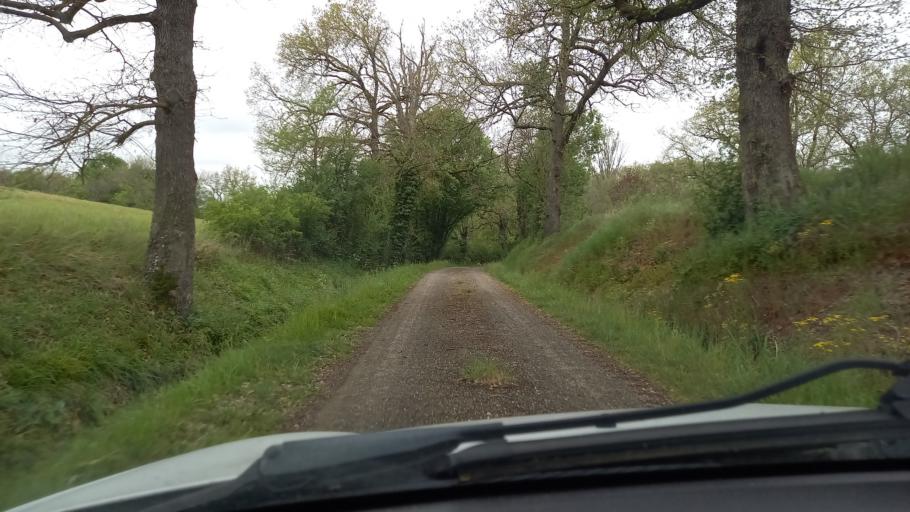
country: FR
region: Midi-Pyrenees
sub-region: Departement du Gers
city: Aubiet
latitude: 43.7598
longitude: 0.8401
